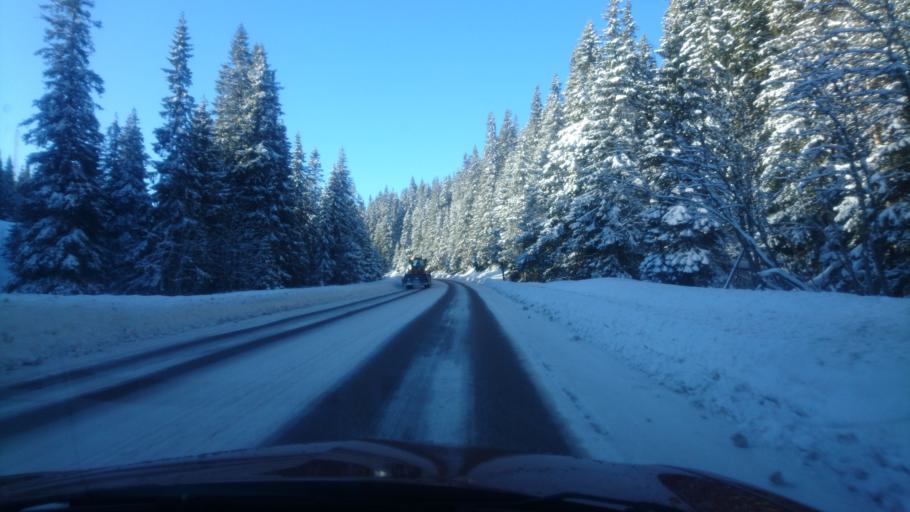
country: SE
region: Dalarna
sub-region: Malung-Saelens kommun
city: Malung
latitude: 61.1671
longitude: 13.1528
